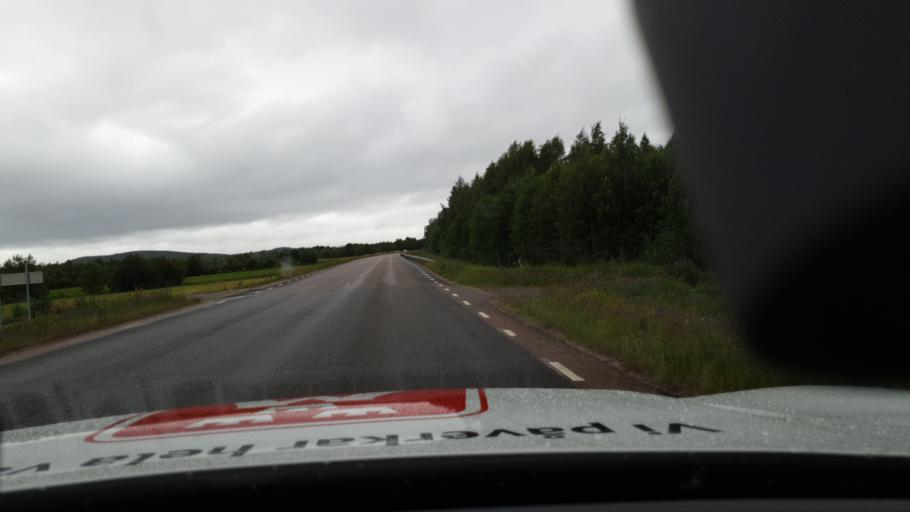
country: SE
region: Norrbotten
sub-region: Overtornea Kommun
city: OEvertornea
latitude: 66.4125
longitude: 23.6244
